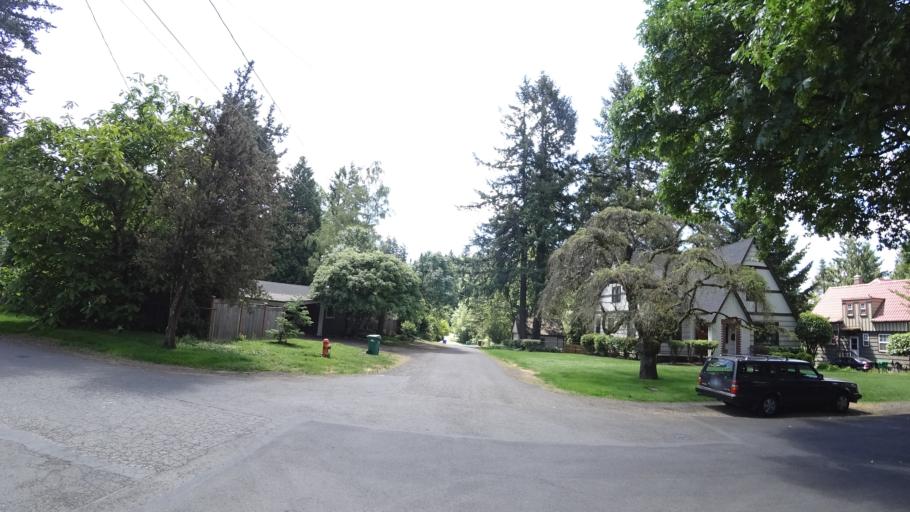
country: US
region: Oregon
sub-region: Washington County
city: Garden Home-Whitford
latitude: 45.4614
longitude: -122.7206
